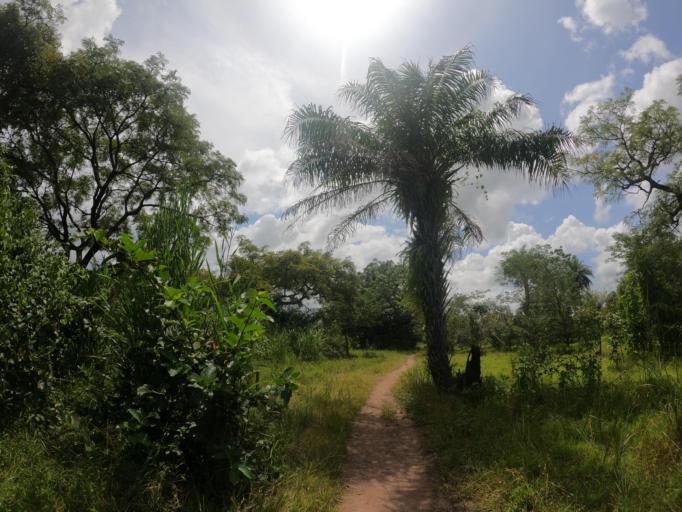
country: SL
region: Northern Province
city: Makeni
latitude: 9.1319
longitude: -12.2748
